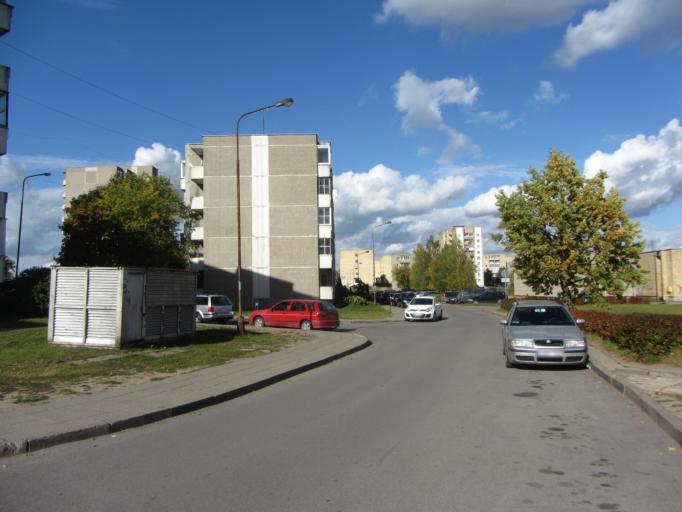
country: LT
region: Utenos apskritis
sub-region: Utena
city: Utena
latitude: 55.4961
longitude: 25.6160
